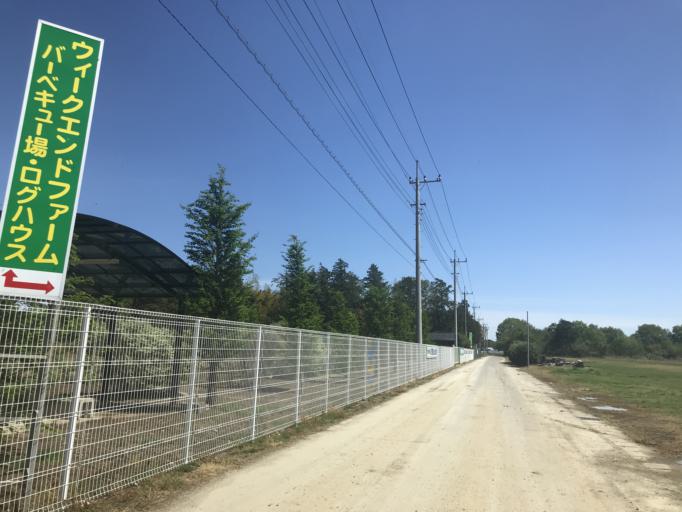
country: JP
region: Ibaraki
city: Shimodate
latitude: 36.2828
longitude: 140.0197
